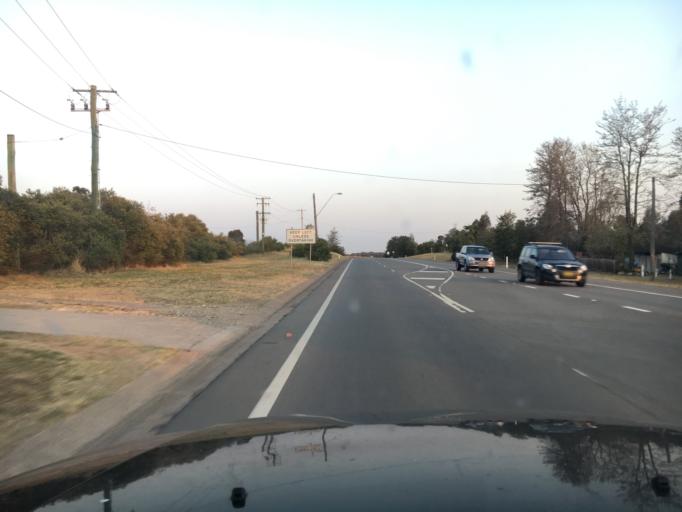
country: AU
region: New South Wales
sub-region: Cessnock
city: Branxton
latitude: -32.6579
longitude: 151.3623
